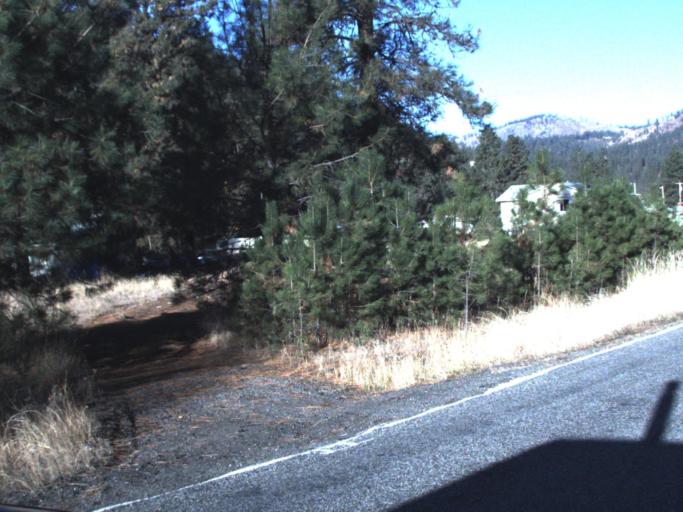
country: US
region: Washington
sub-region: Okanogan County
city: Coulee Dam
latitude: 48.0750
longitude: -118.6800
